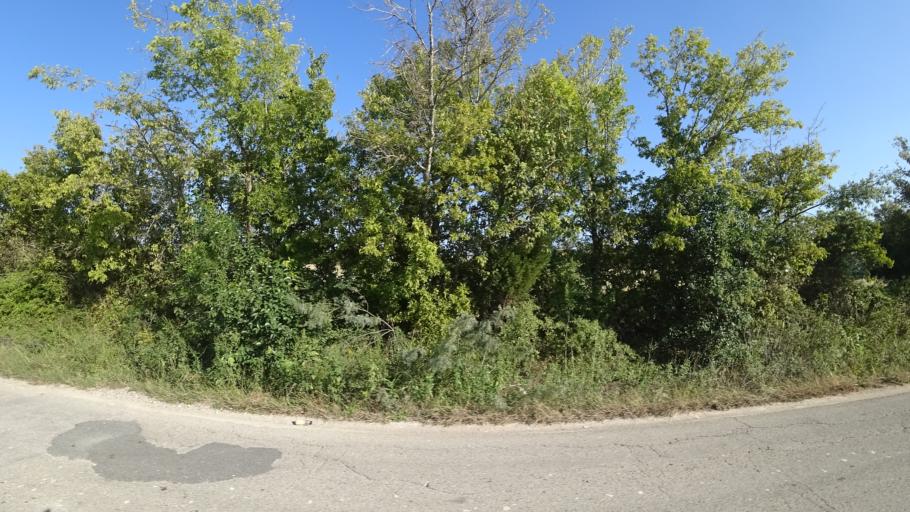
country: US
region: Texas
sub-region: Travis County
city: Wells Branch
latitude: 30.3462
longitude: -97.6733
